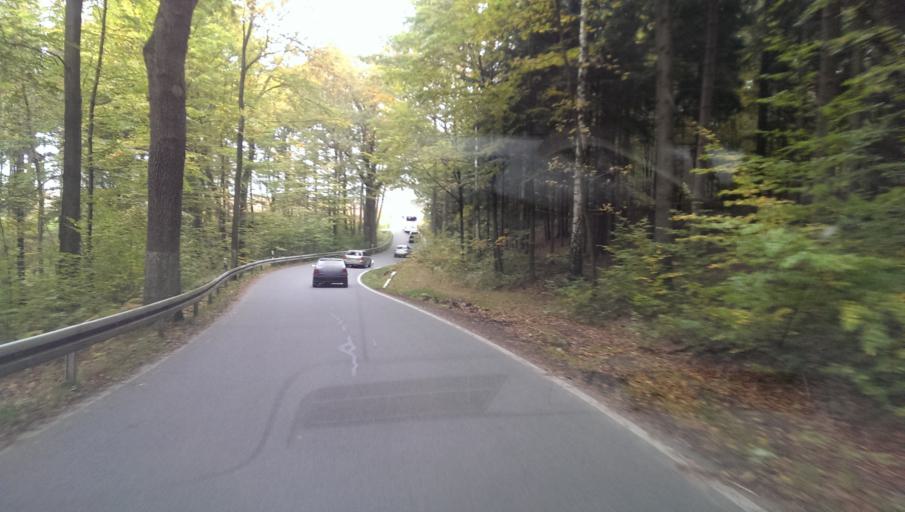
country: DE
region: Saxony
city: Hohnstein
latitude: 50.9747
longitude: 14.0930
